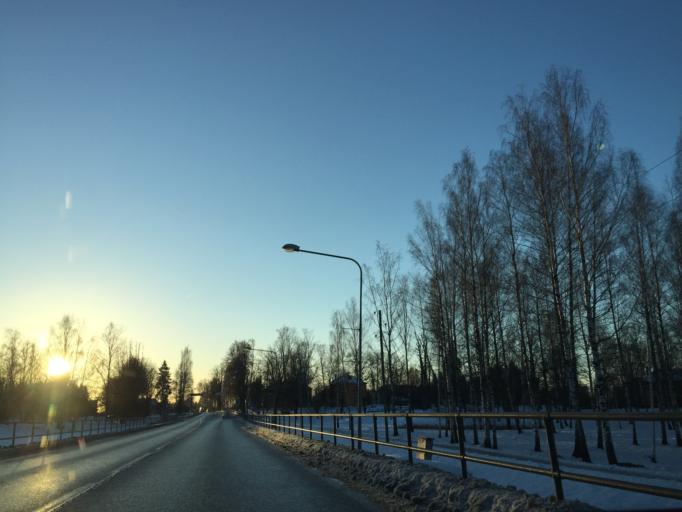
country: LV
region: Kegums
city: Kegums
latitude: 56.7431
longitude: 24.7228
